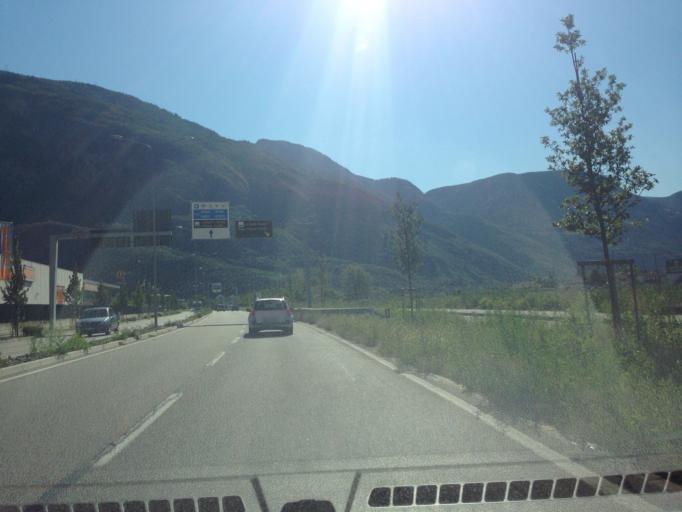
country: IT
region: Trentino-Alto Adige
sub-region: Bolzano
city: San Giacomo
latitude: 46.4698
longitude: 11.3190
